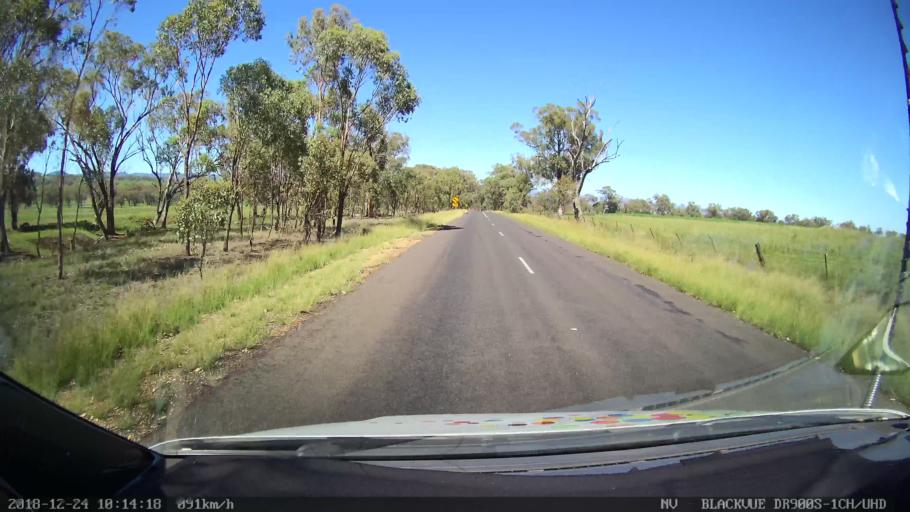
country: AU
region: New South Wales
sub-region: Liverpool Plains
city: Quirindi
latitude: -31.6965
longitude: 150.6300
